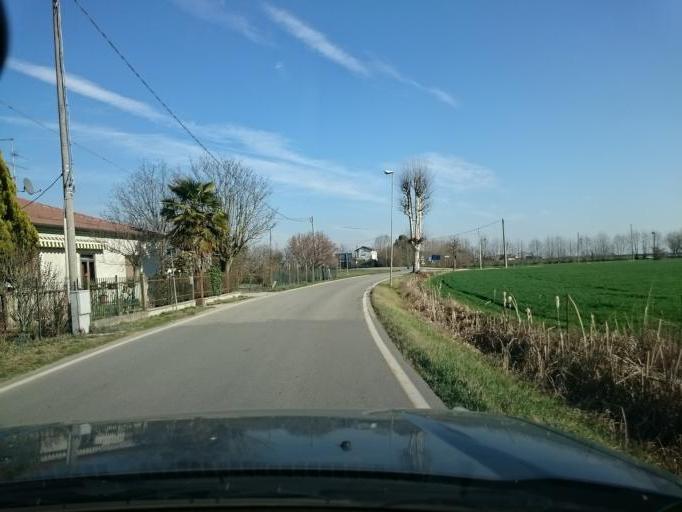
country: IT
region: Veneto
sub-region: Provincia di Verona
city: Isola della Scala
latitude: 45.2705
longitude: 11.0291
